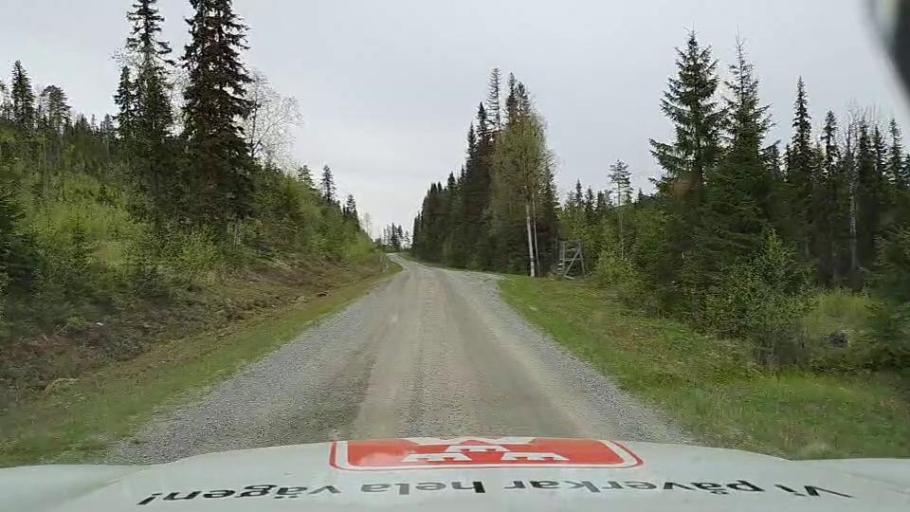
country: SE
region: Jaemtland
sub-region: Bergs Kommun
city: Hoverberg
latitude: 62.5410
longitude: 14.6999
